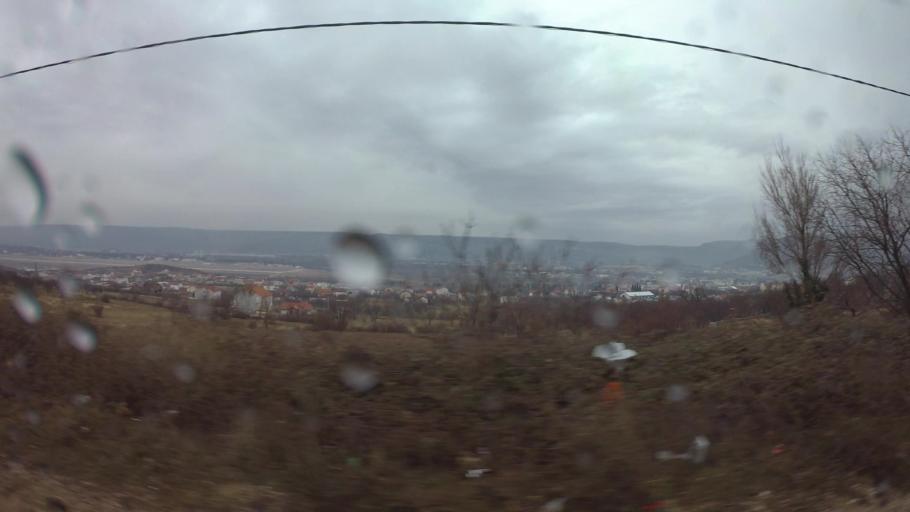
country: BA
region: Federation of Bosnia and Herzegovina
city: Rodoc
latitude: 43.3008
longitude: 17.8543
